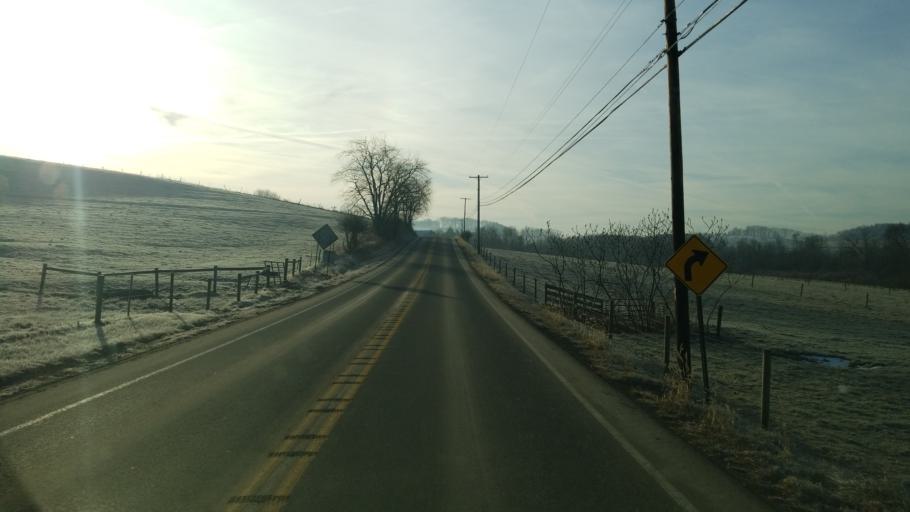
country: US
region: Pennsylvania
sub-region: Indiana County
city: Chevy Chase Heights
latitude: 40.8696
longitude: -79.2371
